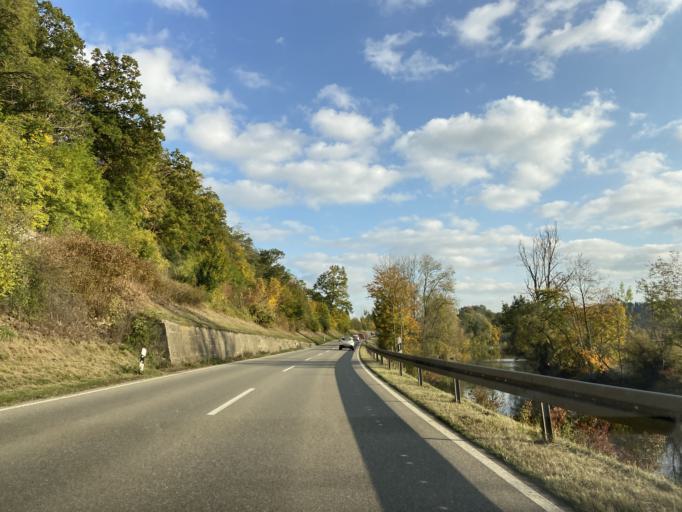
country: DE
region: Baden-Wuerttemberg
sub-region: Tuebingen Region
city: Sigmaringendorf
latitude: 48.0720
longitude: 9.2563
